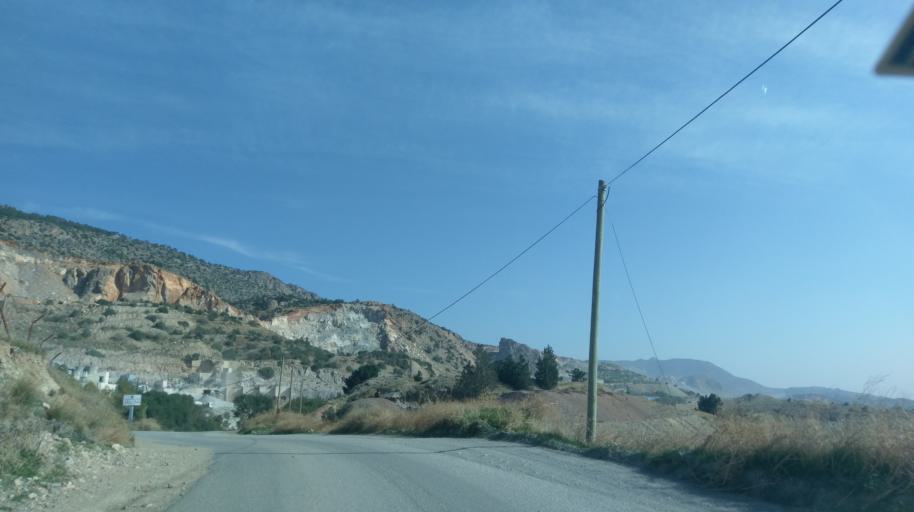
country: CY
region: Lefkosia
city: Nicosia
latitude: 35.2659
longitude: 33.4233
